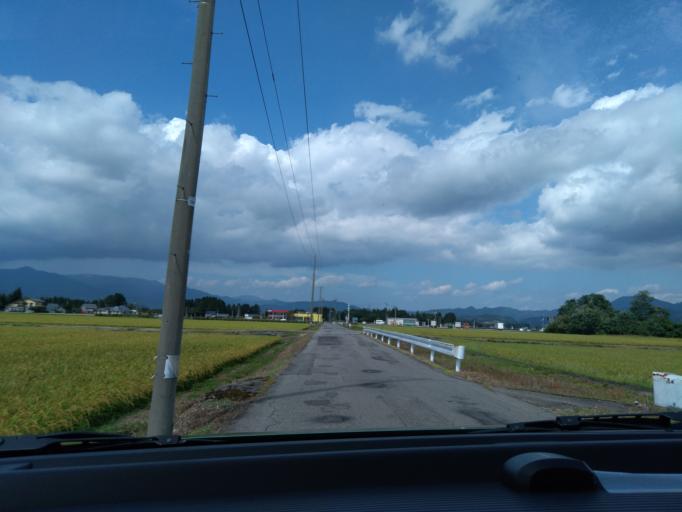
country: JP
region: Akita
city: Kakunodatemachi
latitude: 39.6105
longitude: 140.5843
